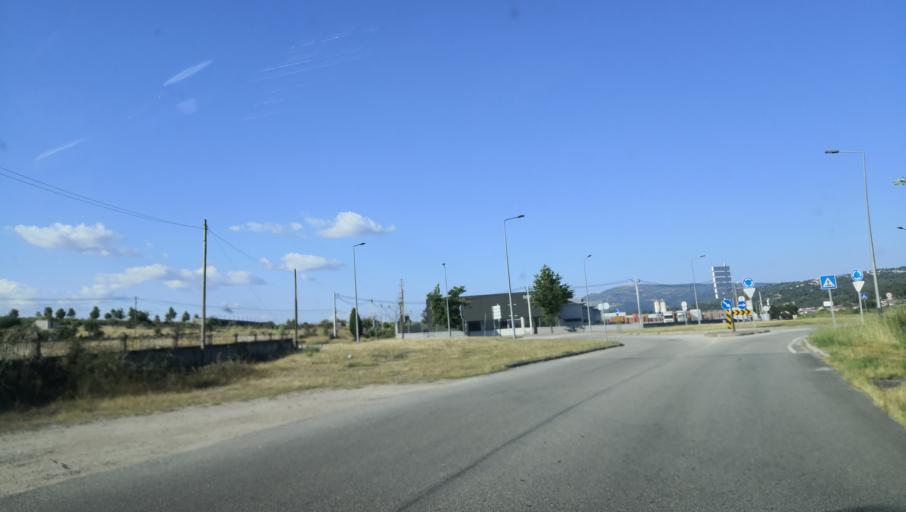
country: PT
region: Vila Real
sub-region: Chaves
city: Chaves
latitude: 41.7803
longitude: -7.4431
